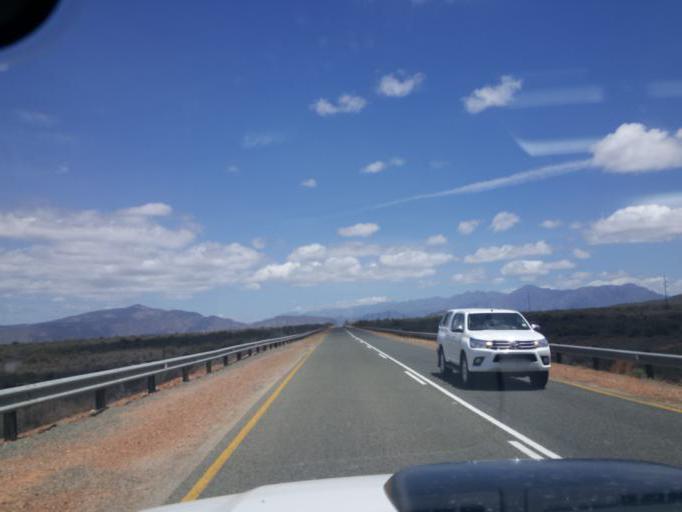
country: ZA
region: Western Cape
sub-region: Central Karoo District Municipality
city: Prince Albert
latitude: -33.5384
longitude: 21.7848
